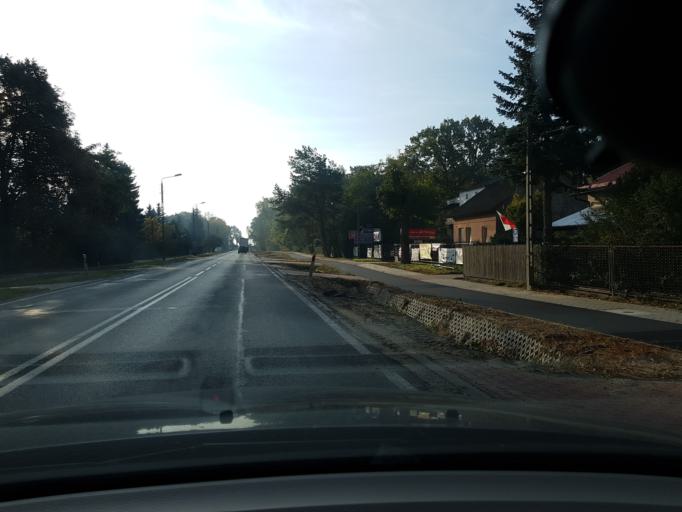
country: PL
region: Masovian Voivodeship
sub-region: Powiat otwocki
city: Jozefow
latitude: 52.1697
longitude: 21.2920
